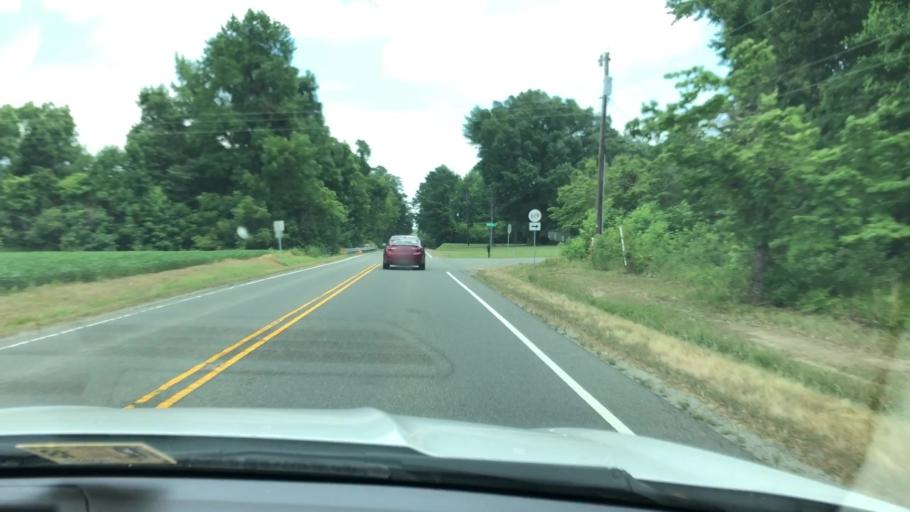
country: US
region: Virginia
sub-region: Lancaster County
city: Lancaster
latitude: 37.7689
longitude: -76.5003
